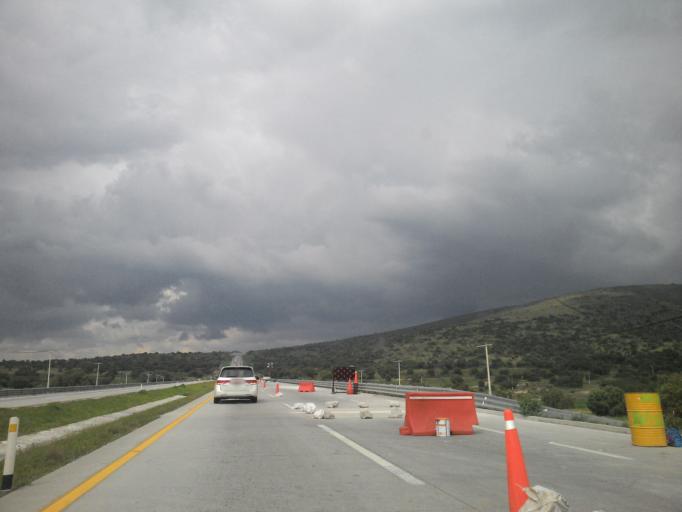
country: MX
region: Mexico
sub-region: Hueypoxtla
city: Santa Maria Ajoloapan
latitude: 19.9576
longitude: -99.0381
